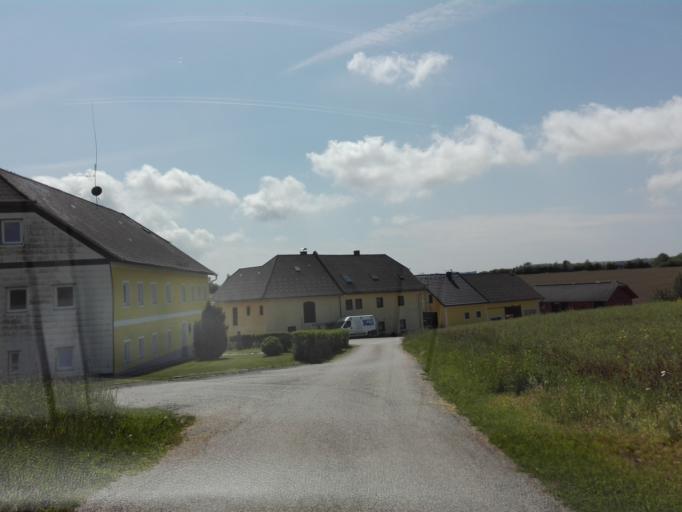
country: AT
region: Upper Austria
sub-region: Politischer Bezirk Rohrbach
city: Atzesberg
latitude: 48.4303
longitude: 13.9116
